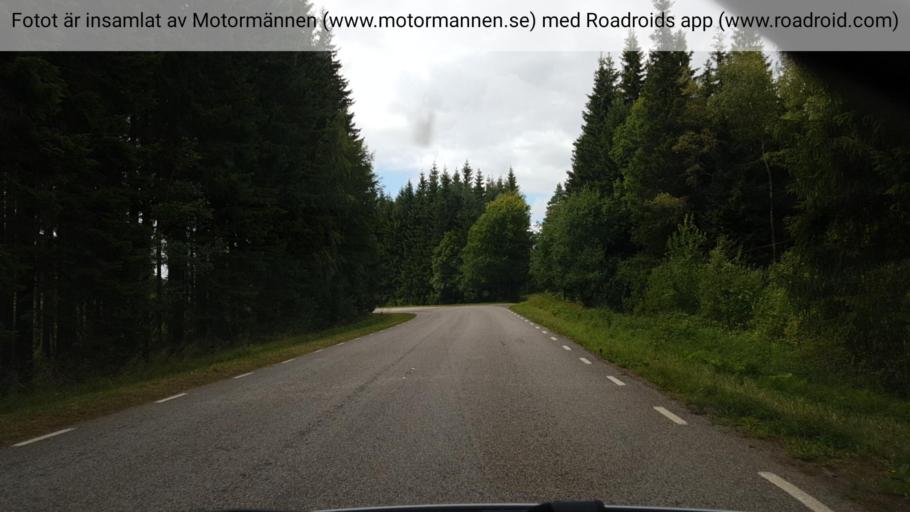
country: SE
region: Vaestra Goetaland
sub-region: Ulricehamns Kommun
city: Ulricehamn
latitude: 57.8039
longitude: 13.5584
